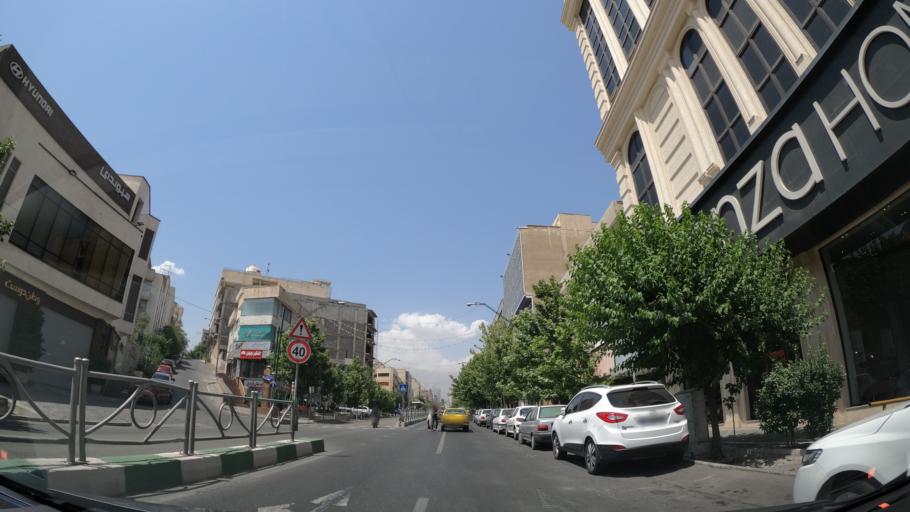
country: IR
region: Tehran
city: Tehran
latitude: 35.7394
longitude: 51.4094
